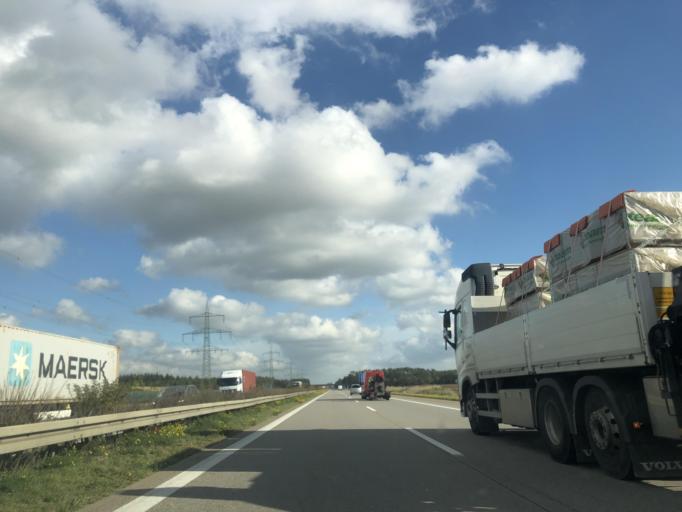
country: DE
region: Mecklenburg-Vorpommern
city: Zarrentin
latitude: 53.5112
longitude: 10.8818
